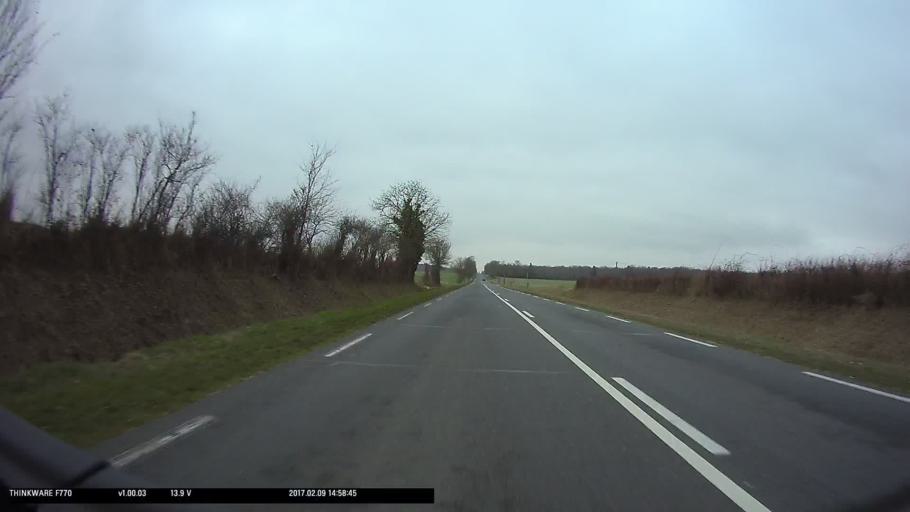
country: FR
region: Centre
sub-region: Departement du Cher
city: Levet
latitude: 46.8349
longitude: 2.4231
